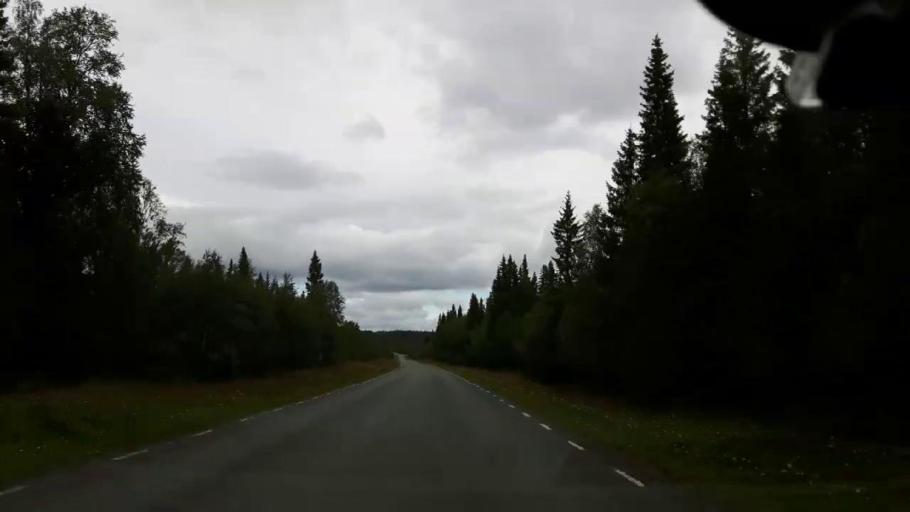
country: SE
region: Jaemtland
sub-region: Krokoms Kommun
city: Valla
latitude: 63.5606
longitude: 13.8480
